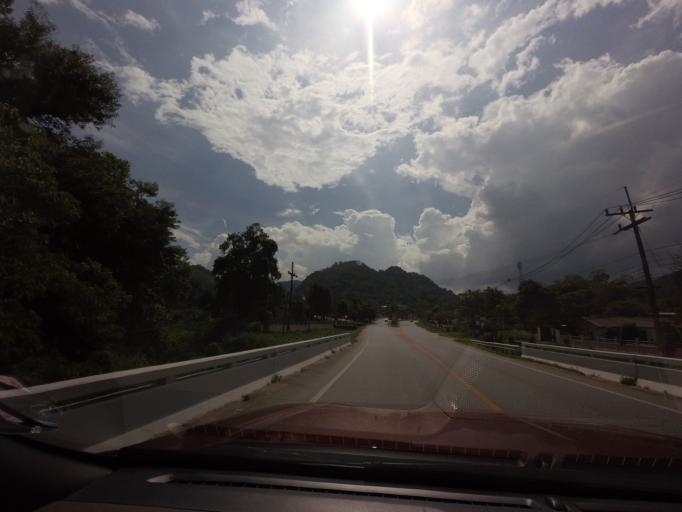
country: TH
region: Yala
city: Than To
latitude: 6.1636
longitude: 101.1834
